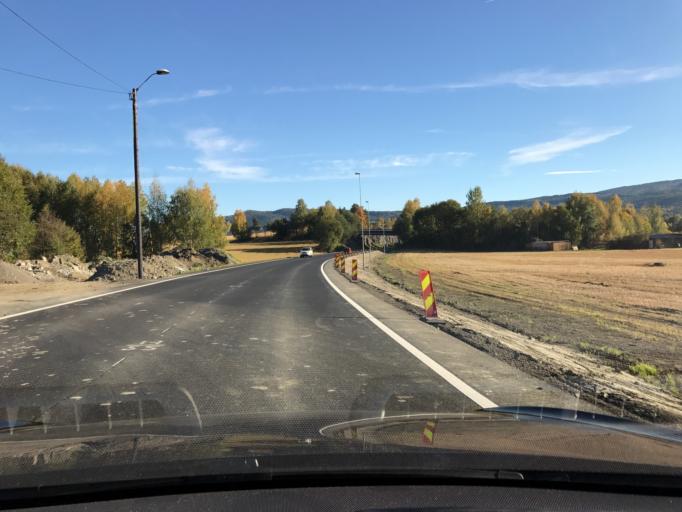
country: NO
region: Buskerud
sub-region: Nedre Eiker
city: Mjondalen
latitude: 59.7627
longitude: 9.9800
